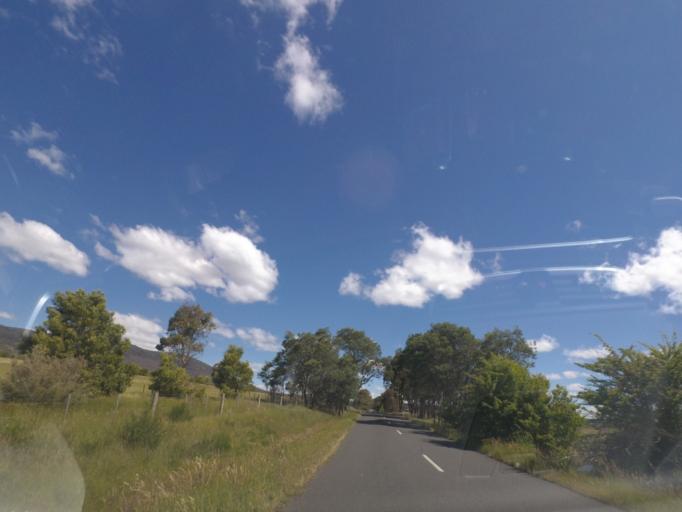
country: AU
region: Victoria
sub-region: Hume
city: Sunbury
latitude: -37.3439
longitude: 144.5566
